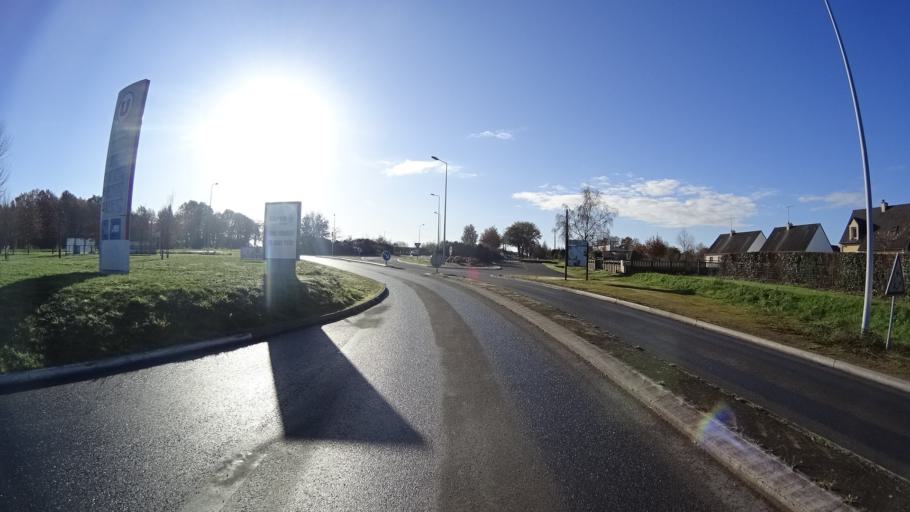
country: FR
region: Brittany
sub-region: Departement du Morbihan
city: Carentoir
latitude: 47.8077
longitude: -2.1302
